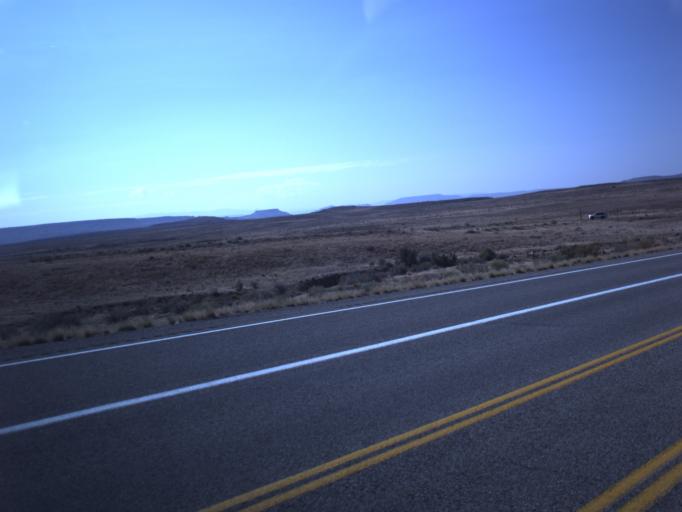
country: US
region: Utah
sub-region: San Juan County
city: Blanding
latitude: 37.4254
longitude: -109.4727
